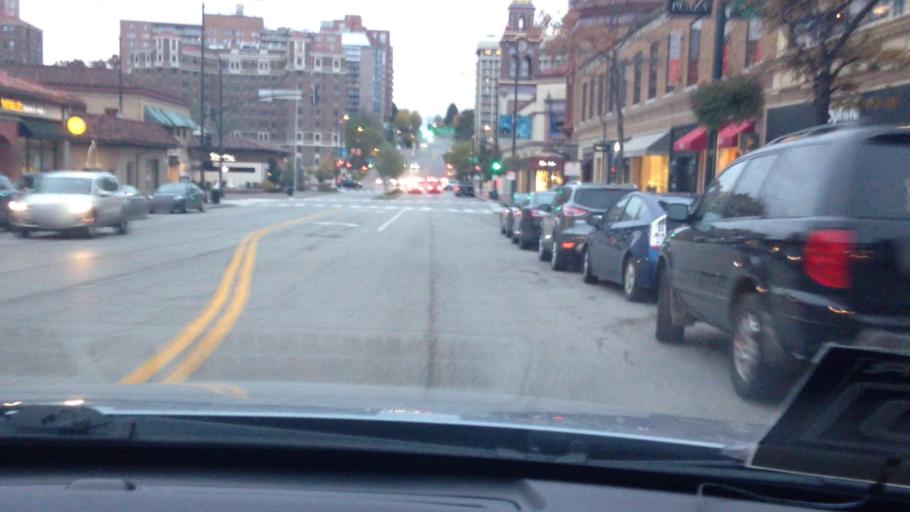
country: US
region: Kansas
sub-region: Johnson County
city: Westwood
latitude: 39.0420
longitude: -94.5917
